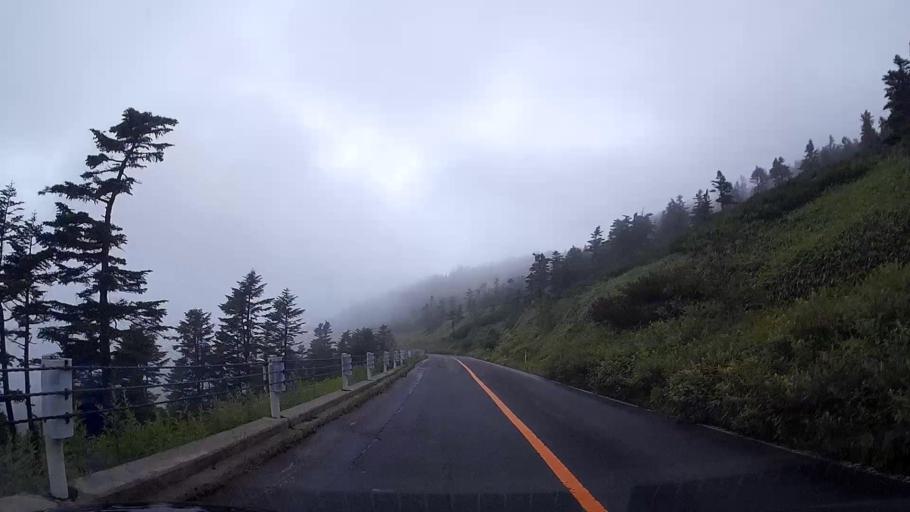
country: JP
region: Nagano
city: Nakano
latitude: 36.6584
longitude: 138.5329
